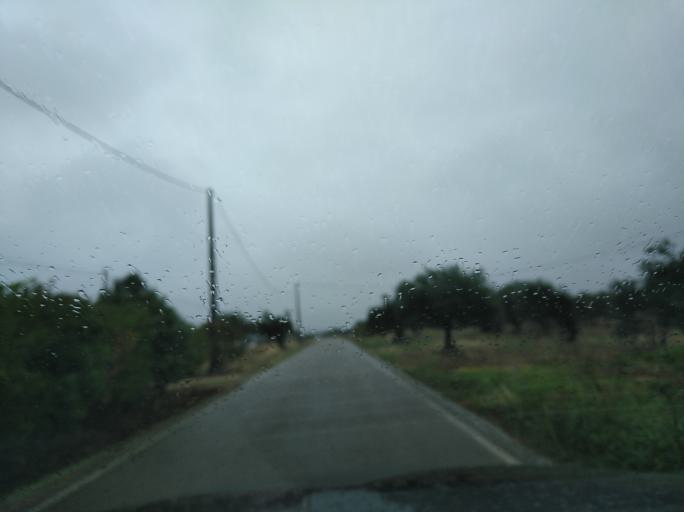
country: PT
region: Portalegre
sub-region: Campo Maior
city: Campo Maior
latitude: 38.9596
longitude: -7.0798
